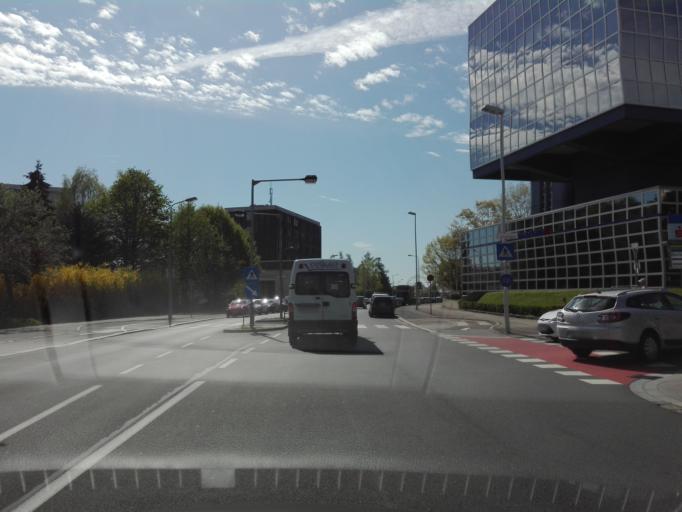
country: AT
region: Upper Austria
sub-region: Linz Stadt
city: Linz
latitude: 48.3165
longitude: 14.2843
